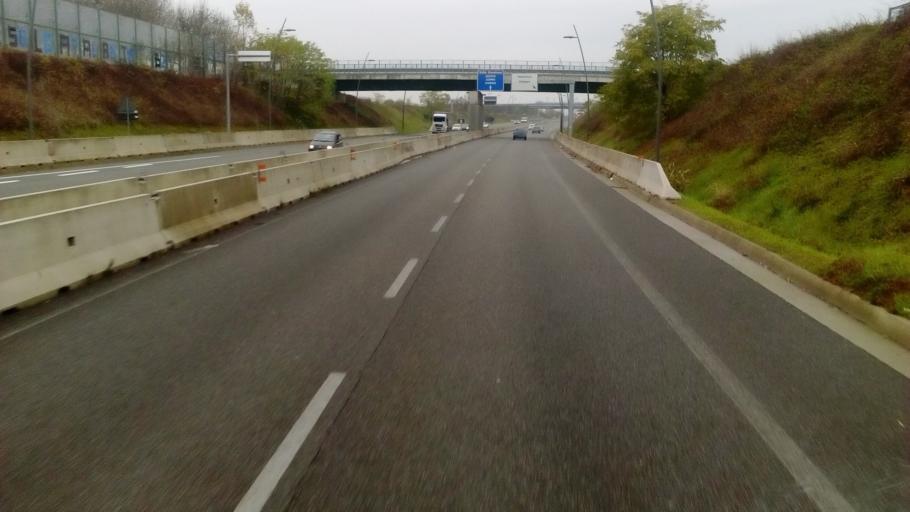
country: IT
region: Lombardy
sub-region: Provincia di Bergamo
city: Dalmine
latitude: 45.6580
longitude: 9.6128
